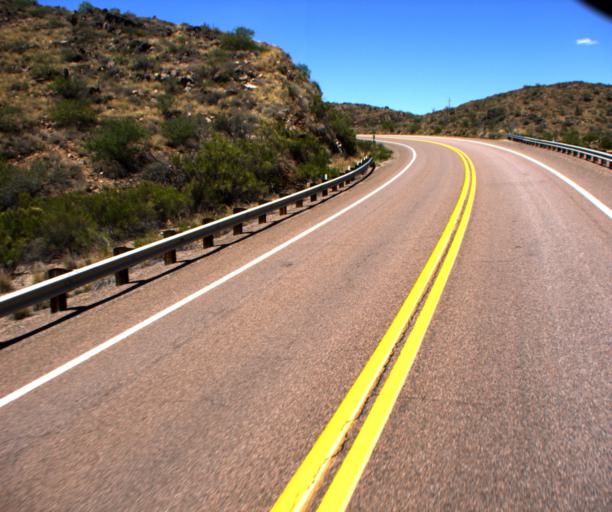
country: US
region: Arizona
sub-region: Yavapai County
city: Bagdad
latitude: 34.5367
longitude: -113.1440
